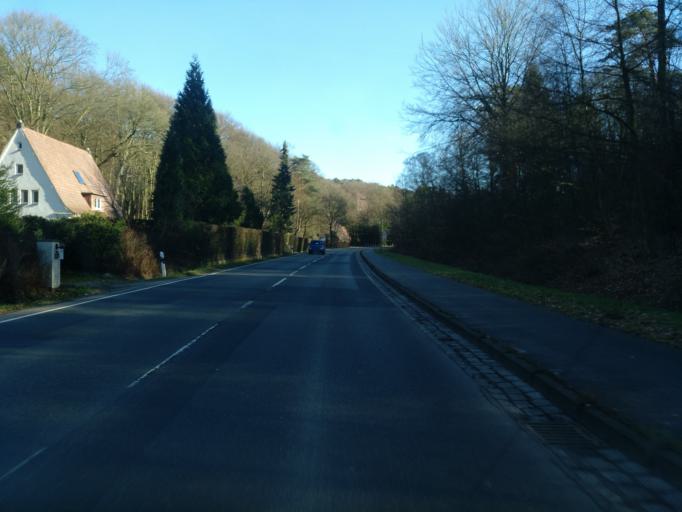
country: DE
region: Hamburg
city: Harburg
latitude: 53.4533
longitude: 9.9023
